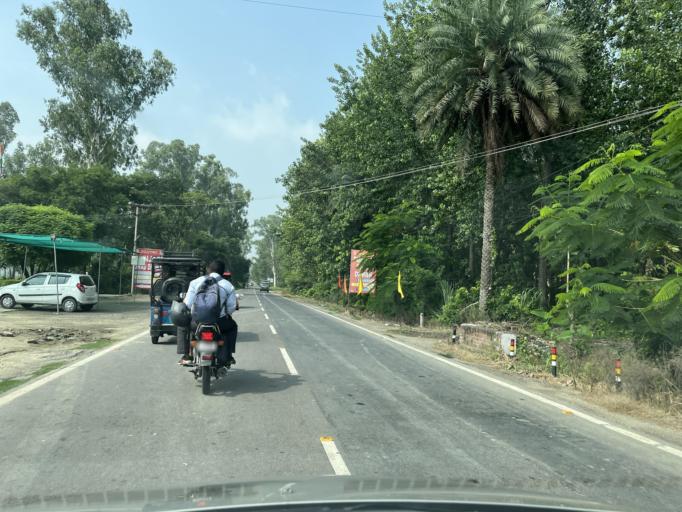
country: IN
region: Uttarakhand
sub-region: Udham Singh Nagar
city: Bazpur
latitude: 29.1768
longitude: 79.1736
